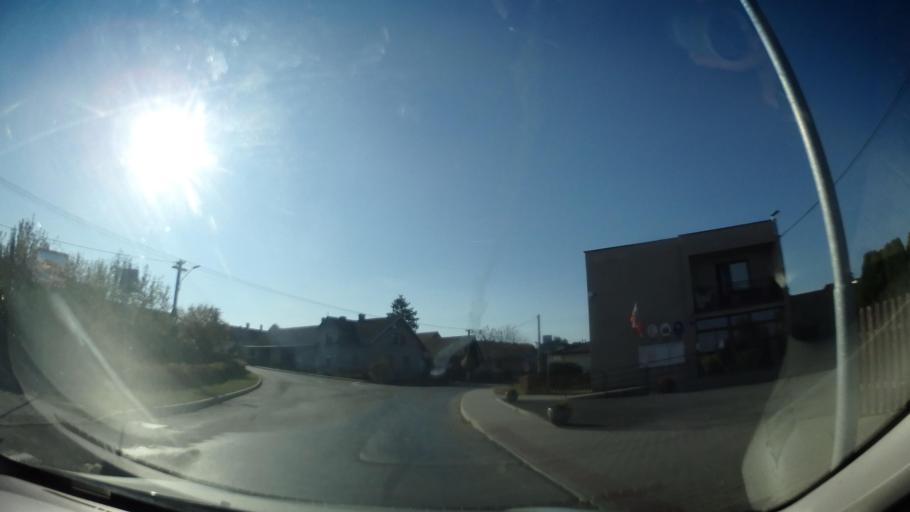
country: CZ
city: Ceske Mezirici
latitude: 50.2494
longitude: 16.0133
